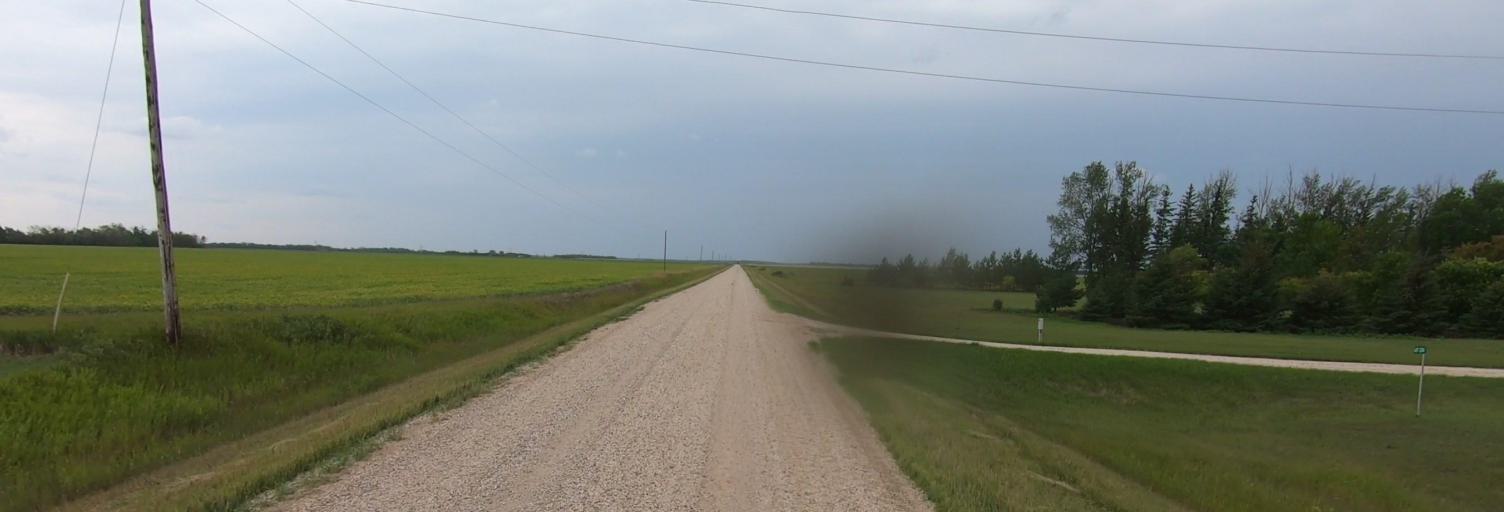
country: CA
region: Manitoba
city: Headingley
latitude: 49.7318
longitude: -97.4136
